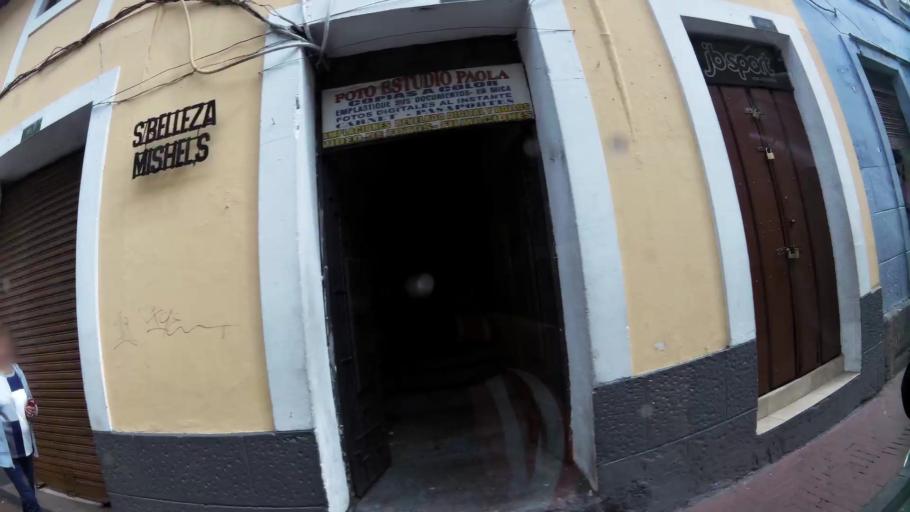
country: EC
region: Pichincha
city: Quito
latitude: -0.2196
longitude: -78.5077
